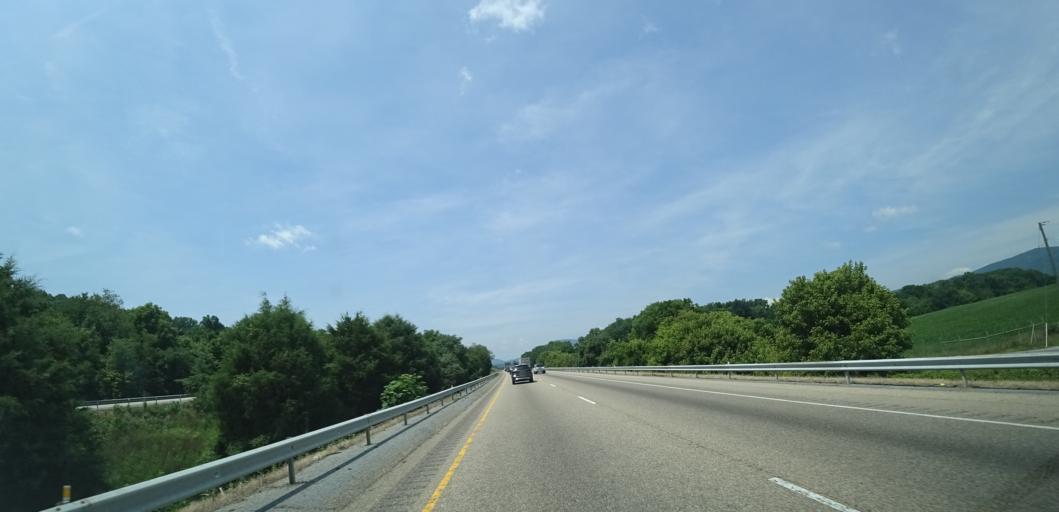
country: US
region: Virginia
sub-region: Rockbridge County
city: Glasgow
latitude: 37.6558
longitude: -79.5407
